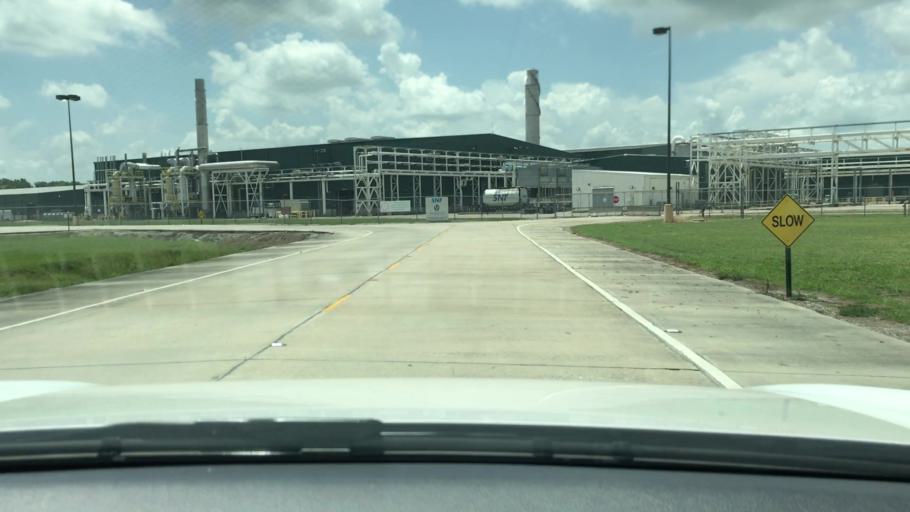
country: US
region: Louisiana
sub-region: Iberville Parish
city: Saint Gabriel
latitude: 30.2692
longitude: -91.1470
